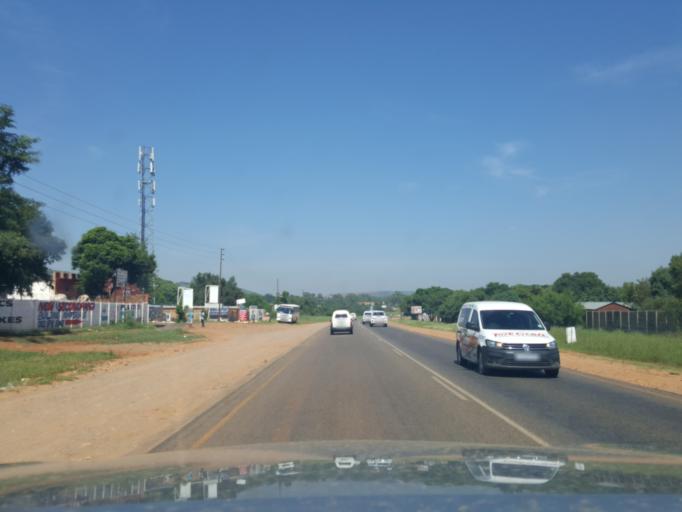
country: ZA
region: Gauteng
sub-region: City of Tshwane Metropolitan Municipality
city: Pretoria
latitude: -25.6771
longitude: 28.3275
